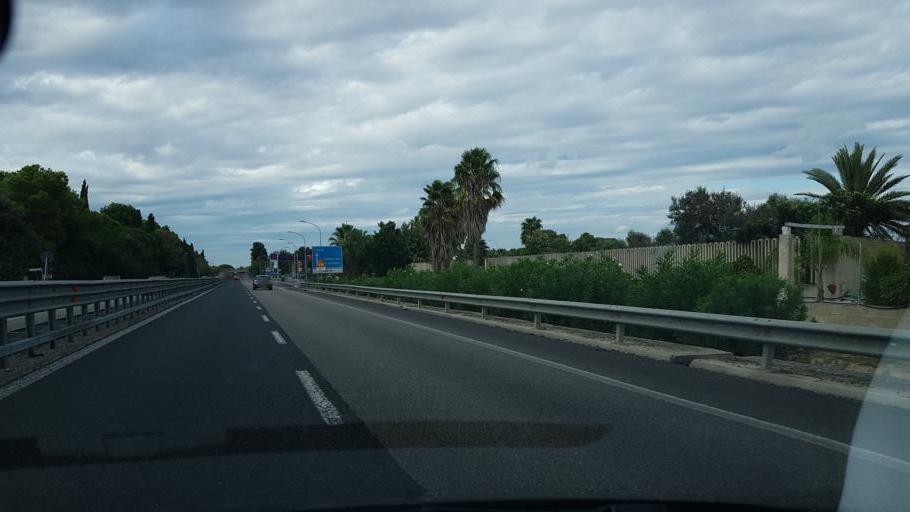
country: IT
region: Apulia
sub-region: Provincia di Lecce
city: Cavallino
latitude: 40.3028
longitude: 18.1925
